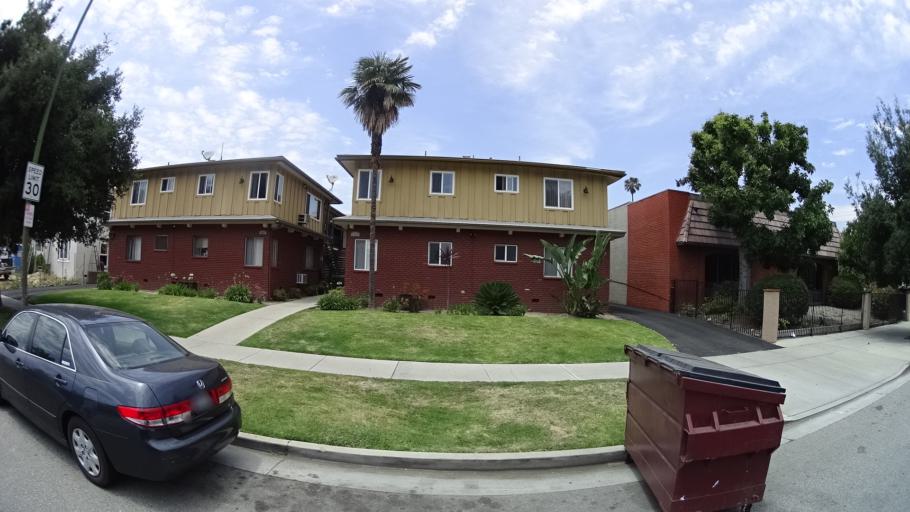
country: US
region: California
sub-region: Los Angeles County
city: Burbank
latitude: 34.1632
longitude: -118.2982
